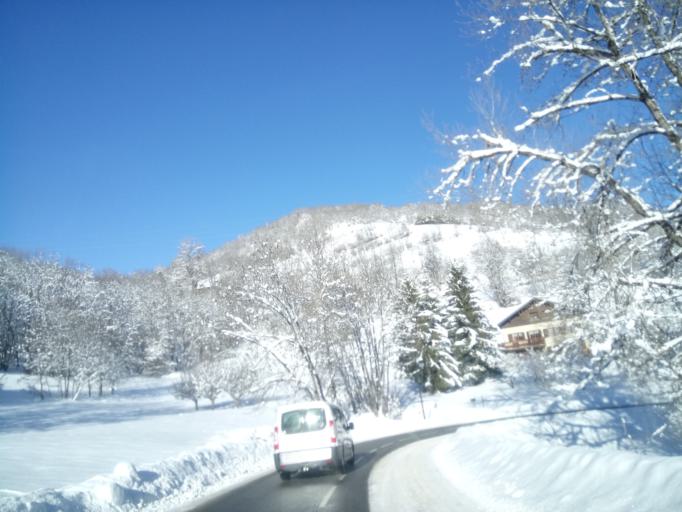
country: FR
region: Rhone-Alpes
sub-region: Departement de la Savoie
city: Saint-Jean-de-Maurienne
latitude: 45.2478
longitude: 6.3023
